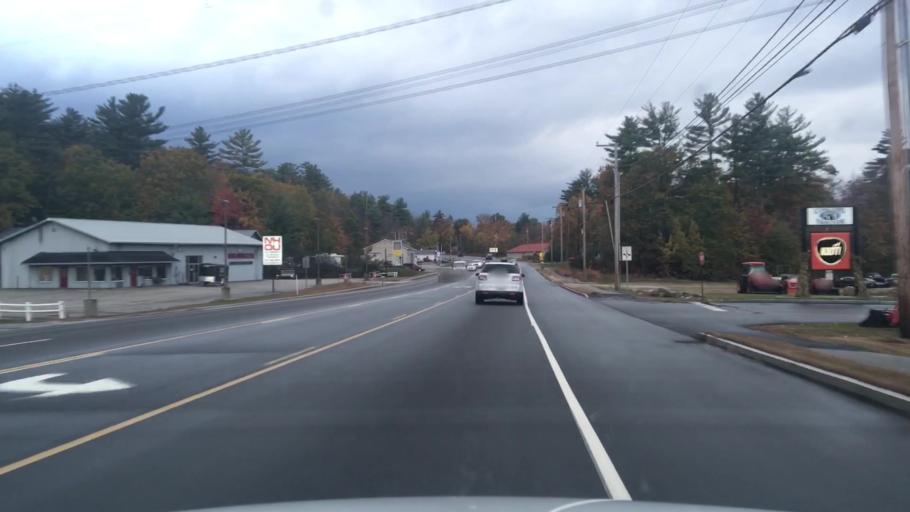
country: US
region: New Hampshire
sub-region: Merrimack County
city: Chichester
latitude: 43.2459
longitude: -71.4084
